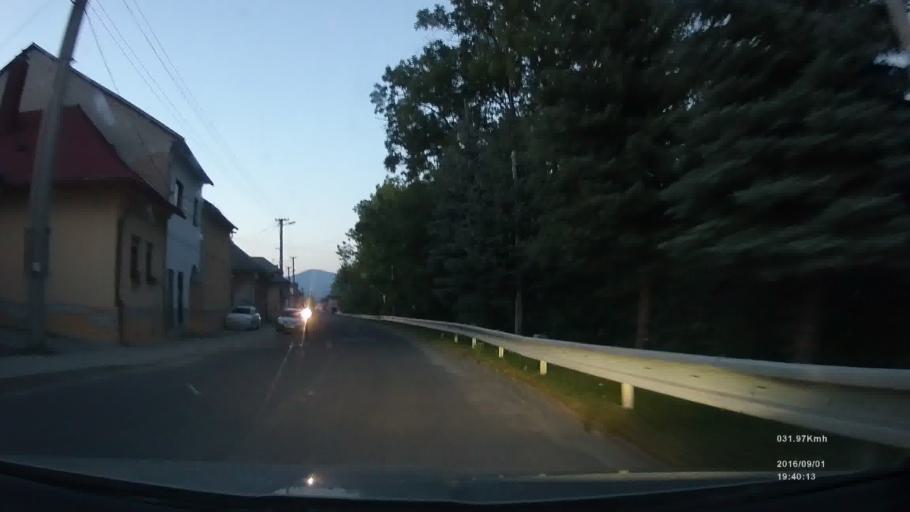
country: SK
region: Zilinsky
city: Ruzomberok
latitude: 49.0597
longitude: 19.4322
